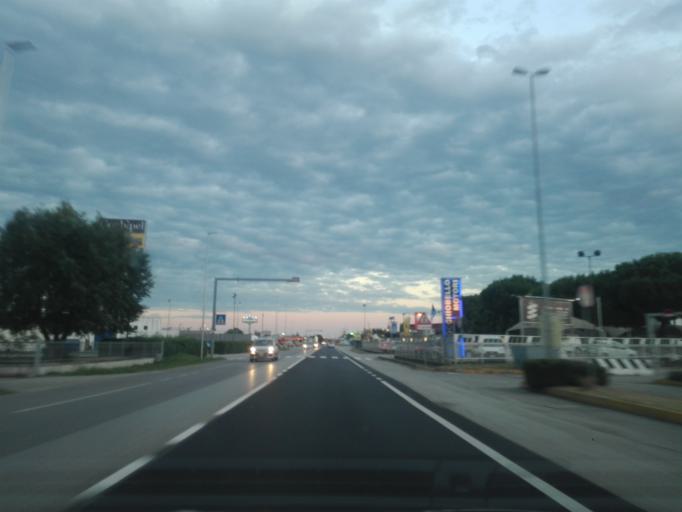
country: IT
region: Veneto
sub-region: Provincia di Rovigo
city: Santa Maria Maddalena
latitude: 44.9153
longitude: 11.5986
